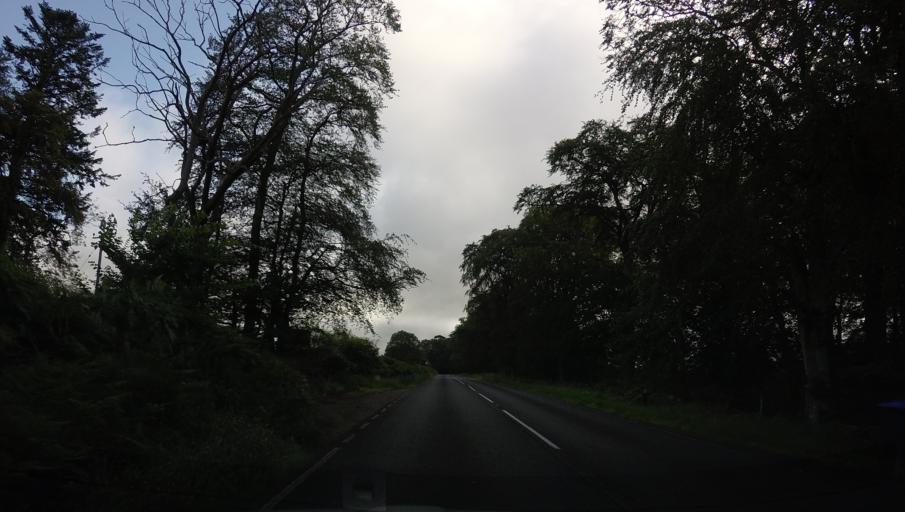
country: GB
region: Scotland
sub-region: Aberdeenshire
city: Westhill
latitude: 57.0721
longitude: -2.3653
